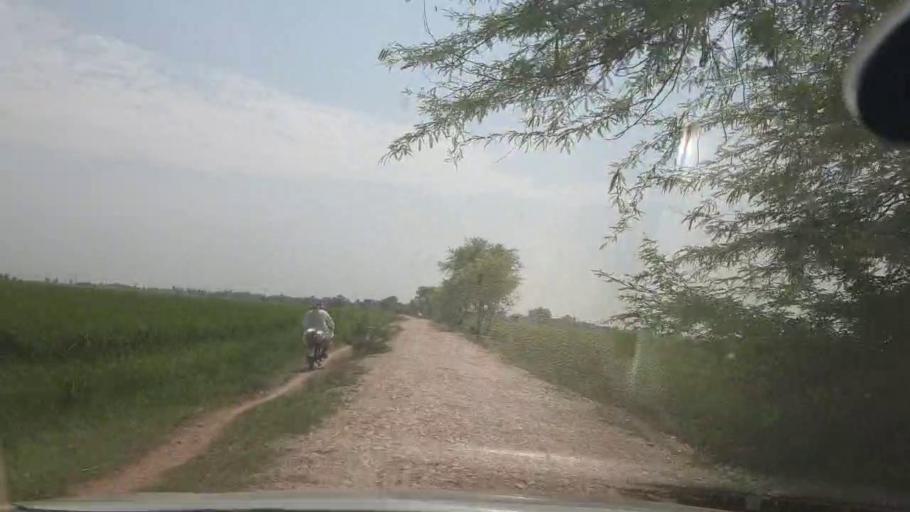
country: PK
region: Sindh
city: Thul
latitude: 28.1652
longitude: 68.6505
